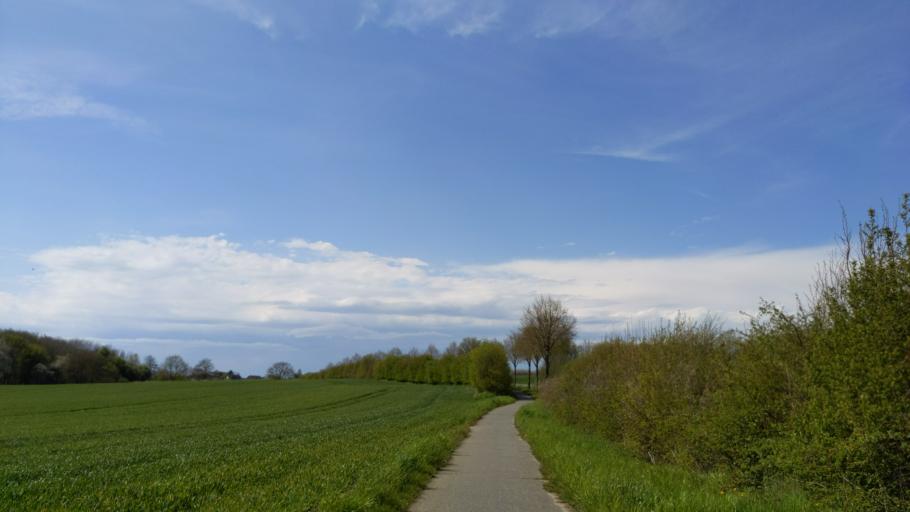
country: DE
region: Schleswig-Holstein
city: Stockelsdorf
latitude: 53.9231
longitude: 10.6574
